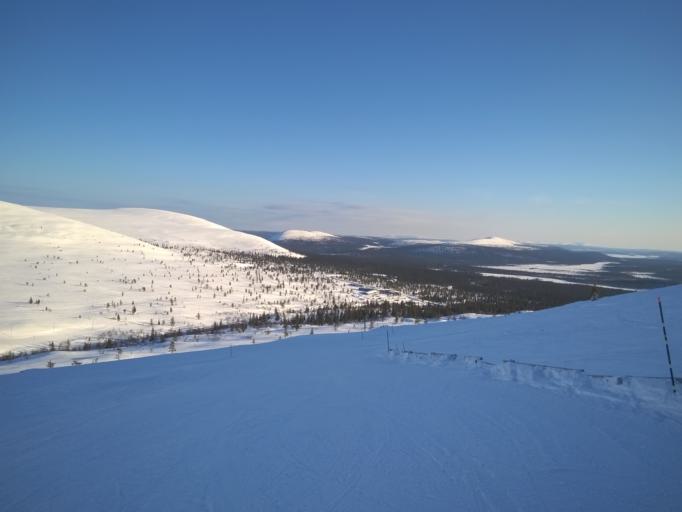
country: FI
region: Lapland
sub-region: Tunturi-Lappi
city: Muonio
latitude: 68.0556
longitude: 24.0500
